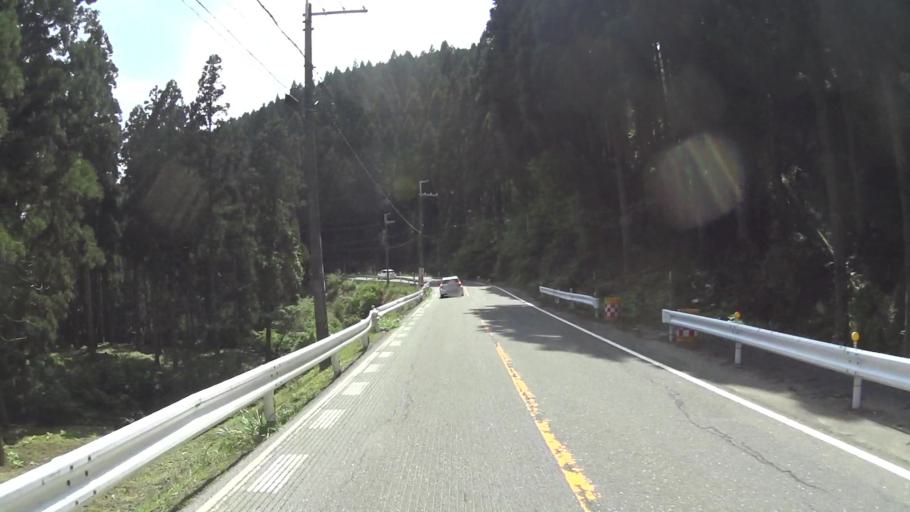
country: JP
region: Fukui
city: Obama
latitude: 35.3800
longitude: 135.9245
